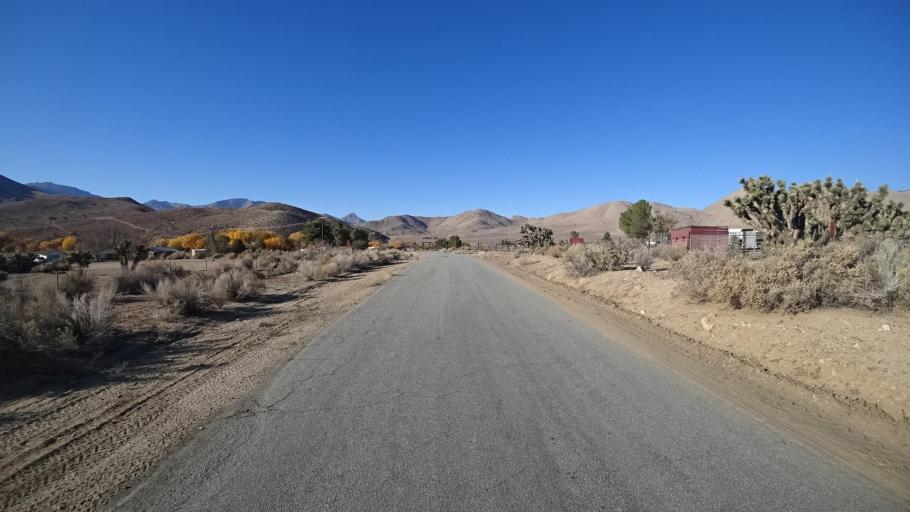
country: US
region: California
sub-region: Kern County
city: Weldon
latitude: 35.5415
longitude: -118.2063
